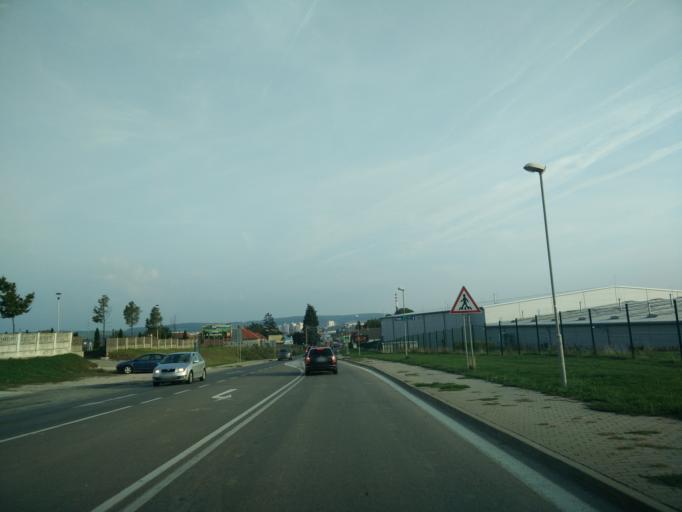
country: SK
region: Nitriansky
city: Banovce nad Bebravou
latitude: 48.7402
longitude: 18.2335
